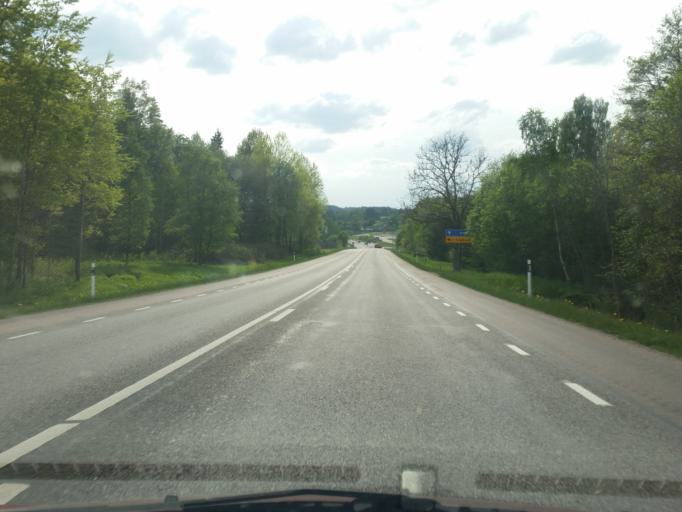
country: SE
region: Vaestra Goetaland
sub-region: Ulricehamns Kommun
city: Ulricehamn
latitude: 57.8093
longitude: 13.2640
